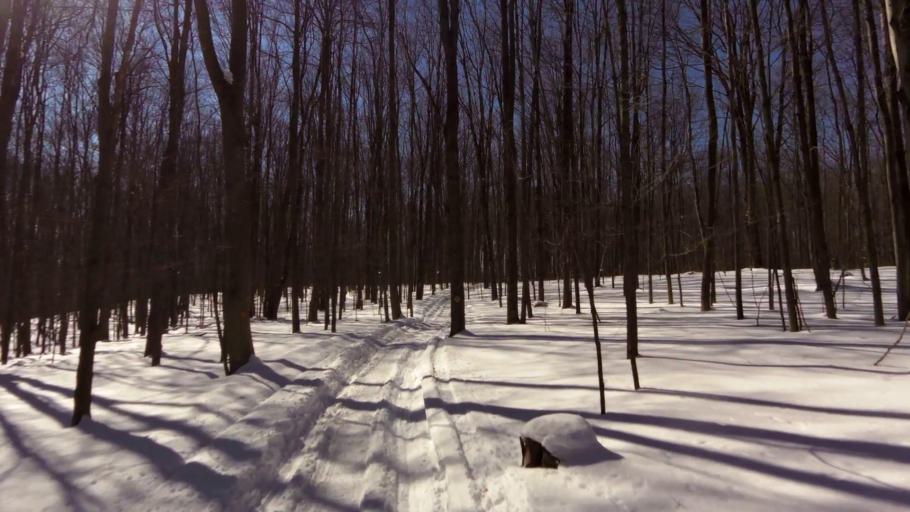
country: US
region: New York
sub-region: Allegany County
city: Cuba
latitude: 42.3180
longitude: -78.2762
